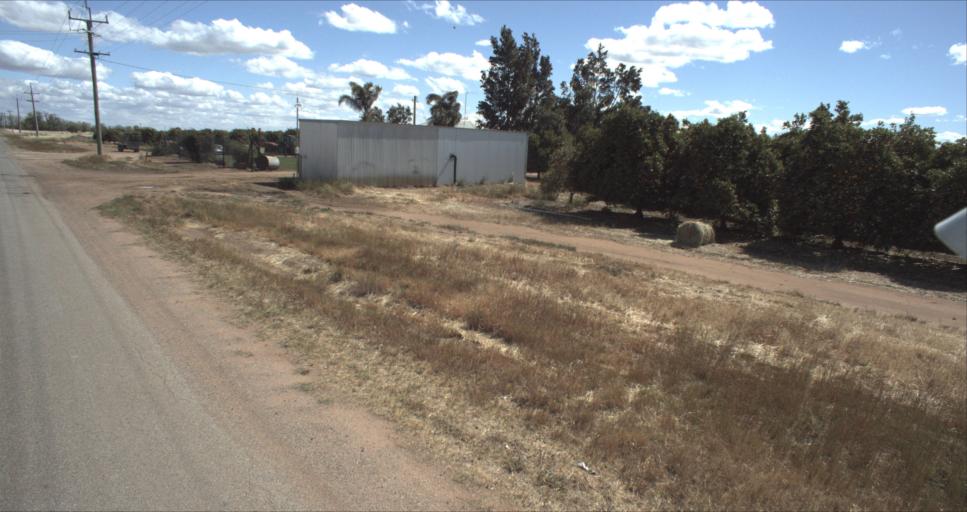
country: AU
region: New South Wales
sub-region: Leeton
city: Leeton
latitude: -34.5105
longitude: 146.2535
